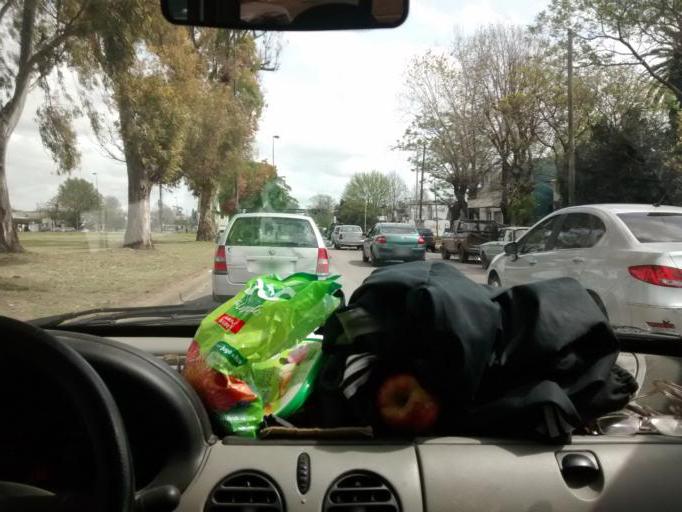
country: AR
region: Buenos Aires
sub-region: Partido de La Plata
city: La Plata
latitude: -34.9392
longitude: -57.9718
